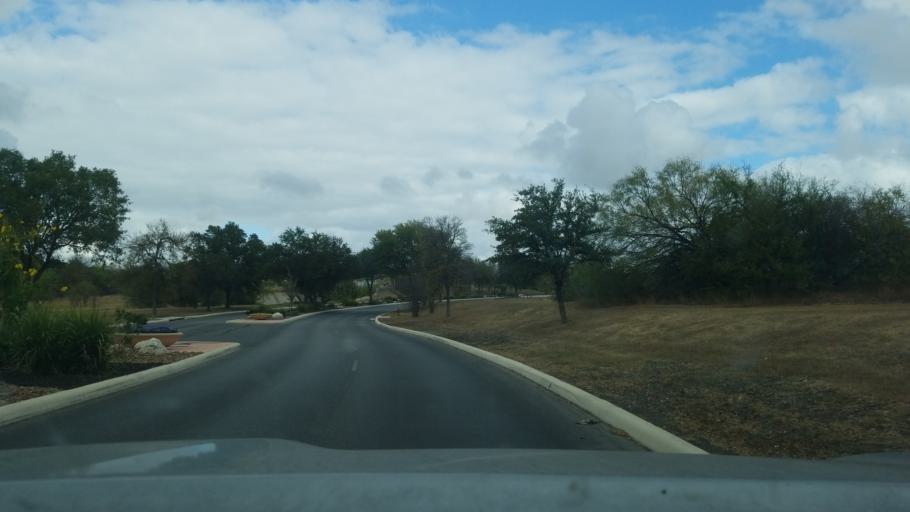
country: US
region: Texas
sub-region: Bexar County
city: Universal City
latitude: 29.5356
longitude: -98.3007
